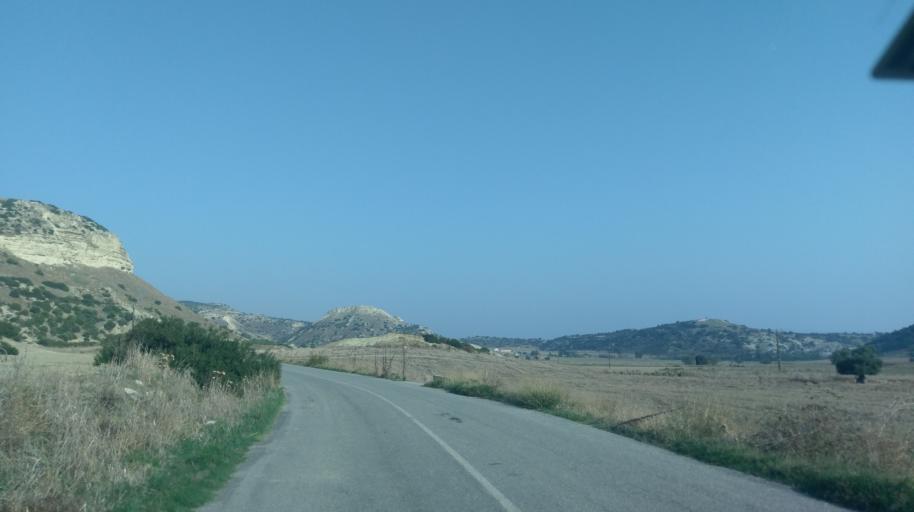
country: CY
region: Ammochostos
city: Rizokarpaso
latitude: 35.5146
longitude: 34.2918
